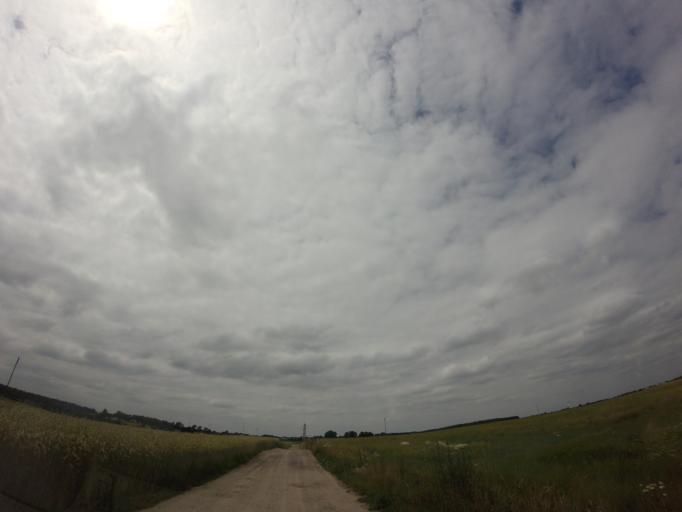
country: PL
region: West Pomeranian Voivodeship
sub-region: Powiat choszczenski
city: Krzecin
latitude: 53.0793
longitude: 15.5116
